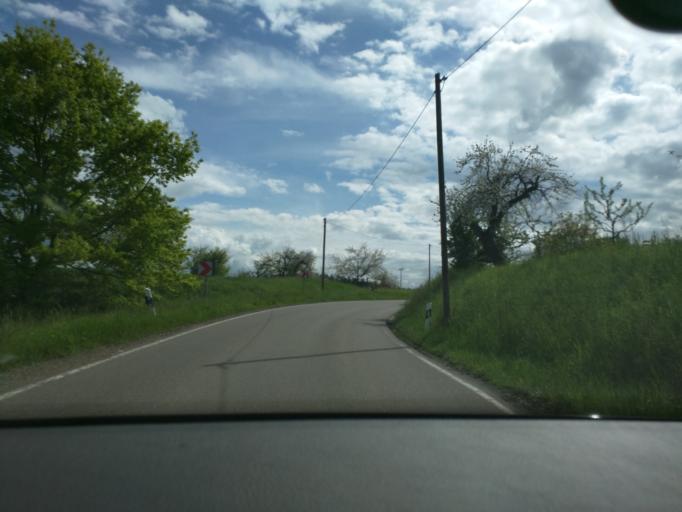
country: DE
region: Baden-Wuerttemberg
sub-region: Tuebingen Region
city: Rottenburg
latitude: 48.5054
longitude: 8.9120
